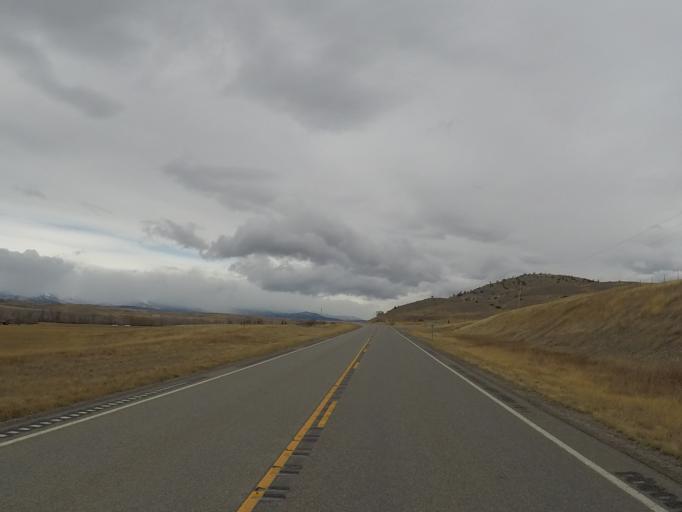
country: US
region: Montana
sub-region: Sweet Grass County
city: Big Timber
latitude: 45.8734
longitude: -109.9482
